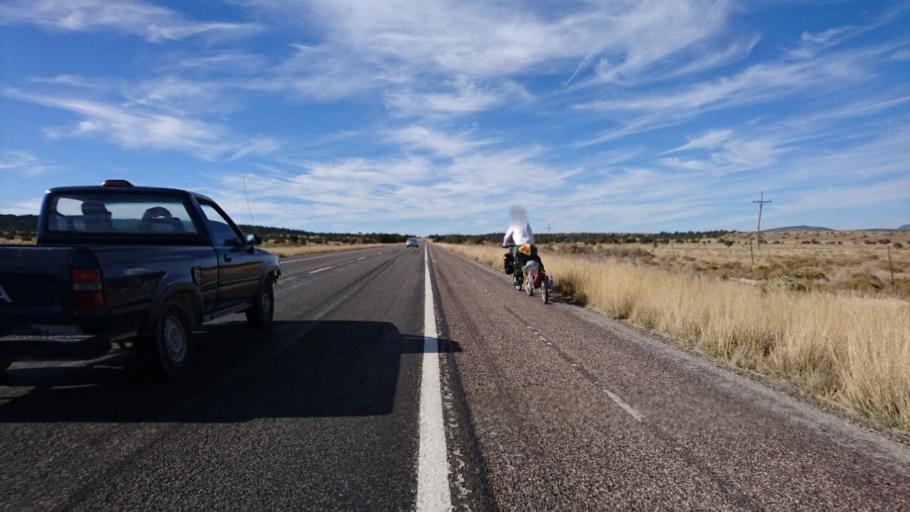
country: US
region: Arizona
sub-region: Mohave County
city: Peach Springs
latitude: 35.5042
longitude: -113.1783
